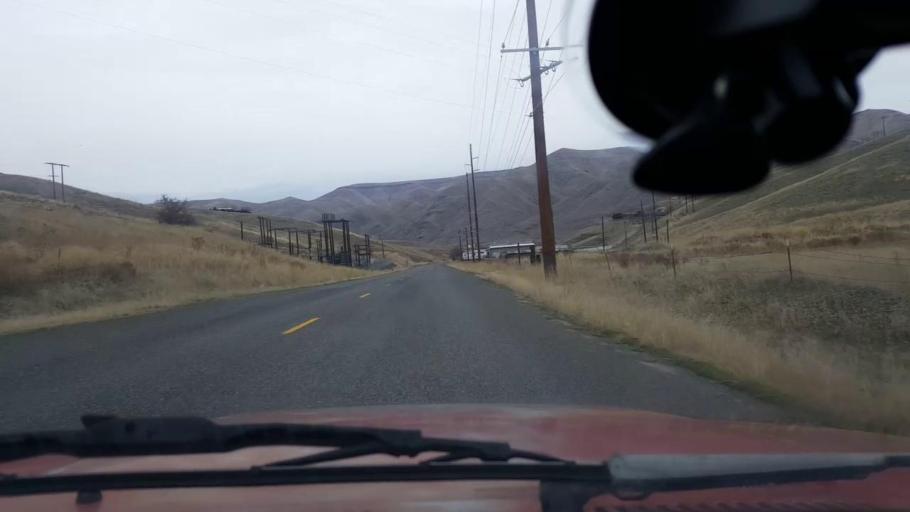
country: US
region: Washington
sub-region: Asotin County
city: Clarkston Heights-Vineland
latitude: 46.4102
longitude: -117.1109
